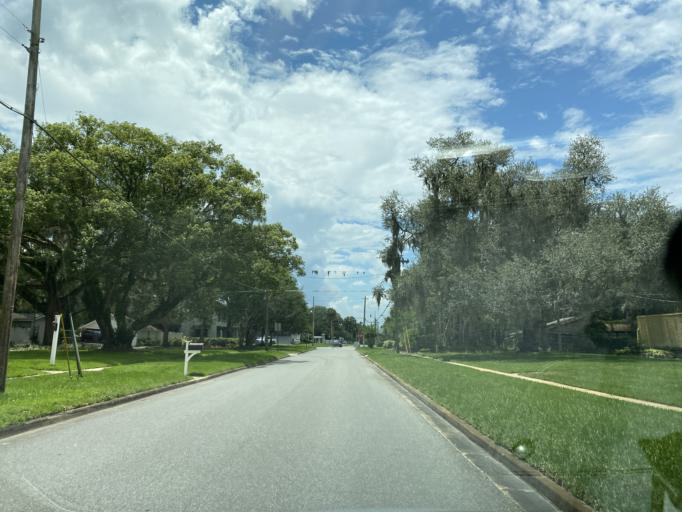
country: US
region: Florida
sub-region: Seminole County
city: Sanford
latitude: 28.8099
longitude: -81.2538
